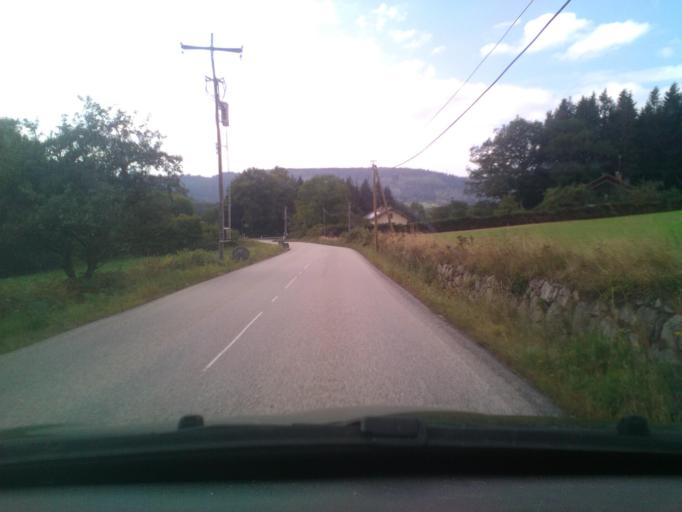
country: FR
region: Lorraine
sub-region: Departement des Vosges
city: Granges-sur-Vologne
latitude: 48.1417
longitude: 6.8210
